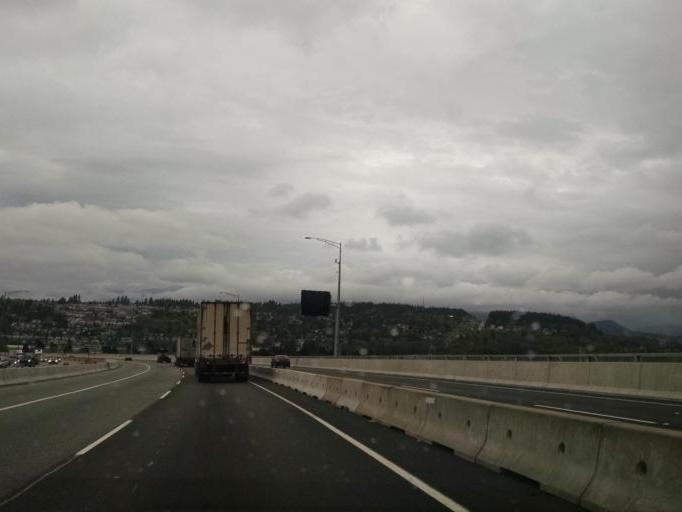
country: CA
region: British Columbia
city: Port Moody
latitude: 49.2232
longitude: -122.8146
